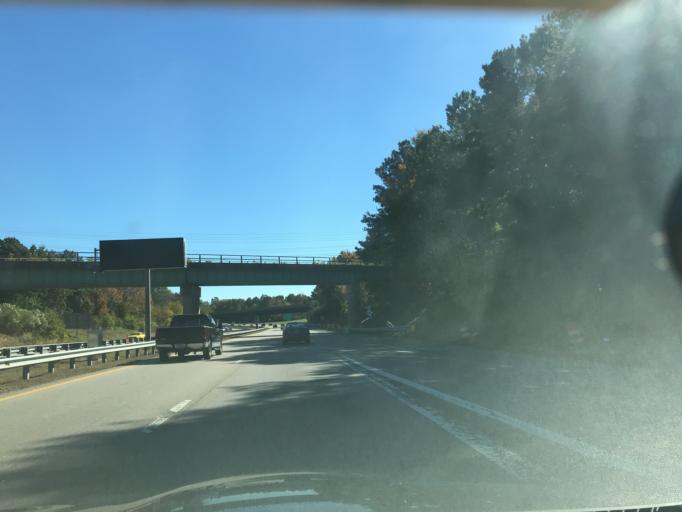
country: US
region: North Carolina
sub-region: Durham County
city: Durham
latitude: 36.0112
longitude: -78.9340
